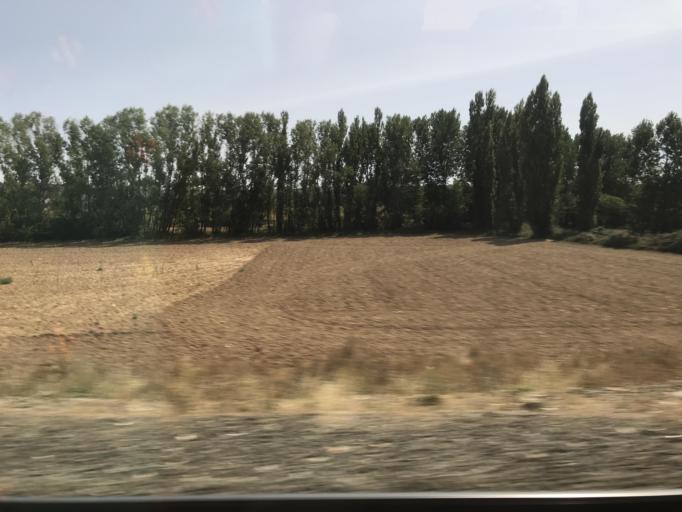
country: ES
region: Castille and Leon
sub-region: Provincia de Palencia
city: Soto de Cerrato
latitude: 41.9830
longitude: -4.4251
